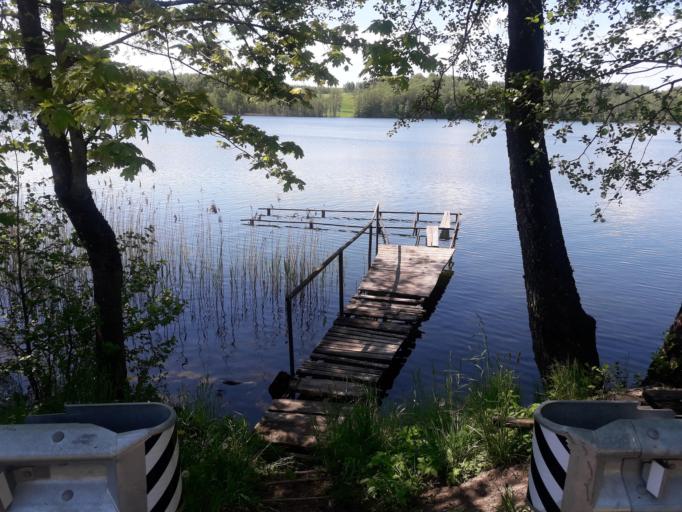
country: LT
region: Alytaus apskritis
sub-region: Alytaus rajonas
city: Daugai
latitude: 54.3839
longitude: 24.2915
